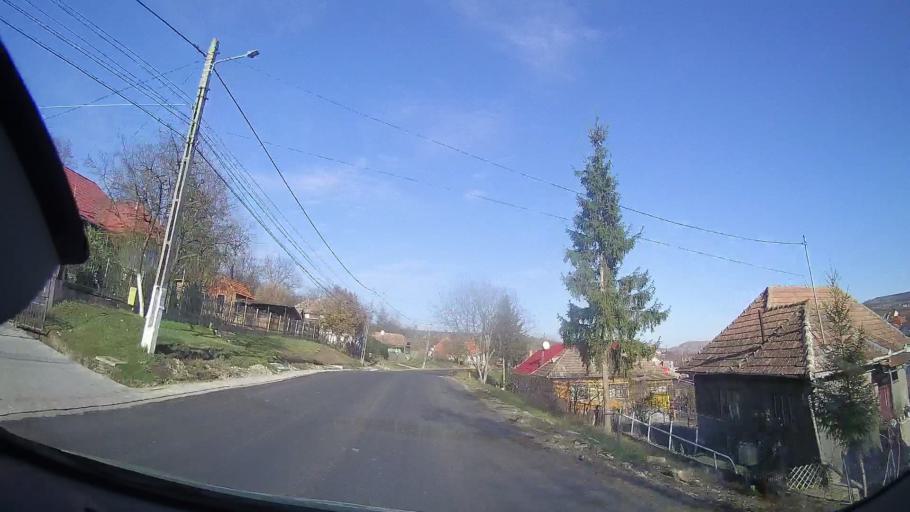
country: RO
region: Mures
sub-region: Comuna Zau De Campie
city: Zau de Campie
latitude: 46.6123
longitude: 24.1237
